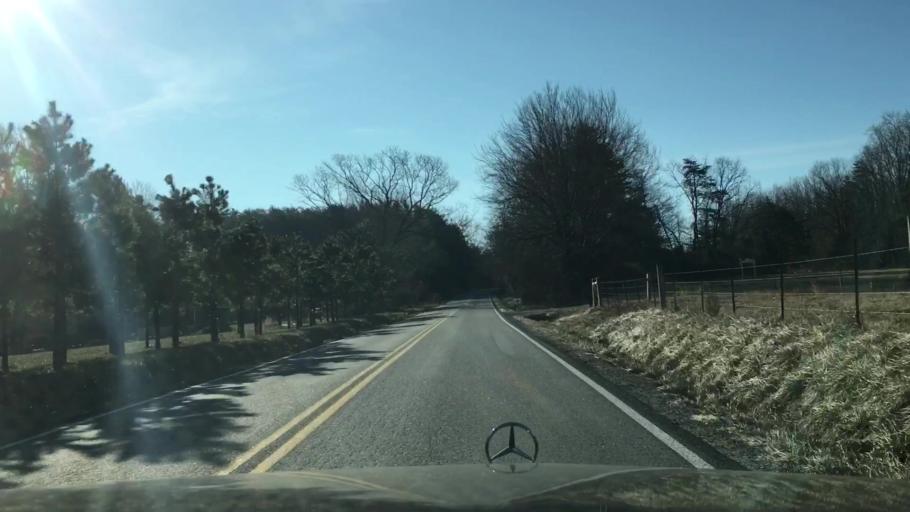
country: US
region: Virginia
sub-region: City of Bedford
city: Bedford
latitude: 37.2112
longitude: -79.4305
